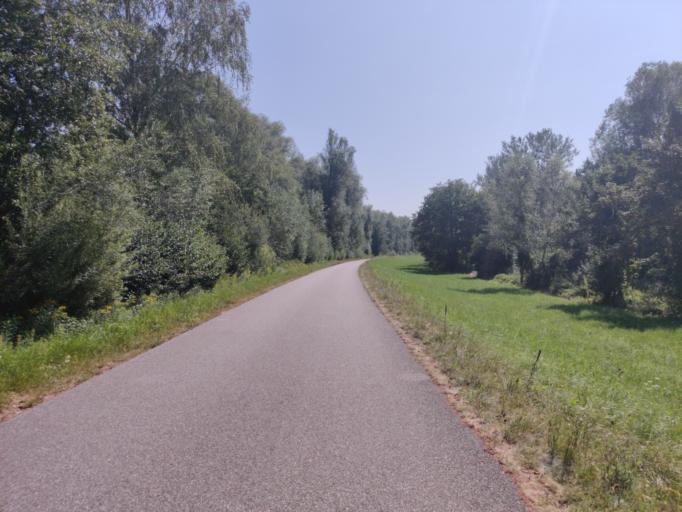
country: AT
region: Upper Austria
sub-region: Politischer Bezirk Urfahr-Umgebung
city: Feldkirchen an der Donau
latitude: 48.3237
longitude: 14.0523
